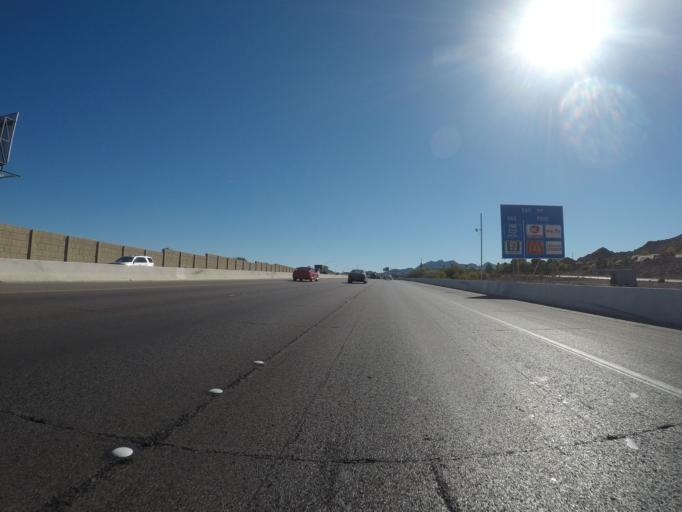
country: US
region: Nevada
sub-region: Clark County
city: Henderson
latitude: 36.0179
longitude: -114.9964
